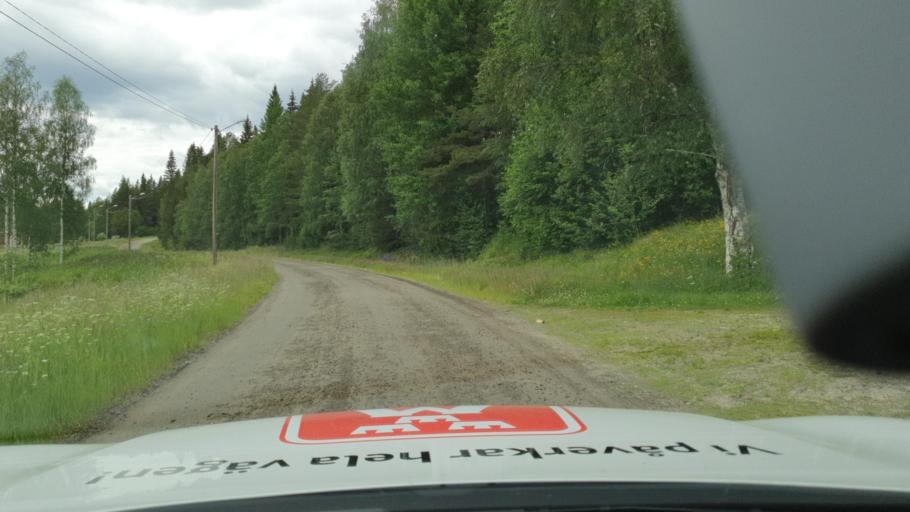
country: SE
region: Vaesterbotten
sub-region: Bjurholms Kommun
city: Bjurholm
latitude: 63.8123
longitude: 19.0445
